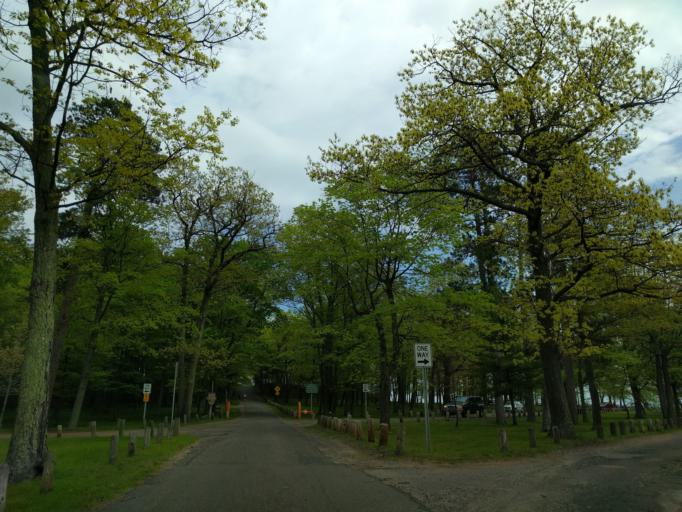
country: US
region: Michigan
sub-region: Marquette County
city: Marquette
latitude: 46.5810
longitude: -87.3827
